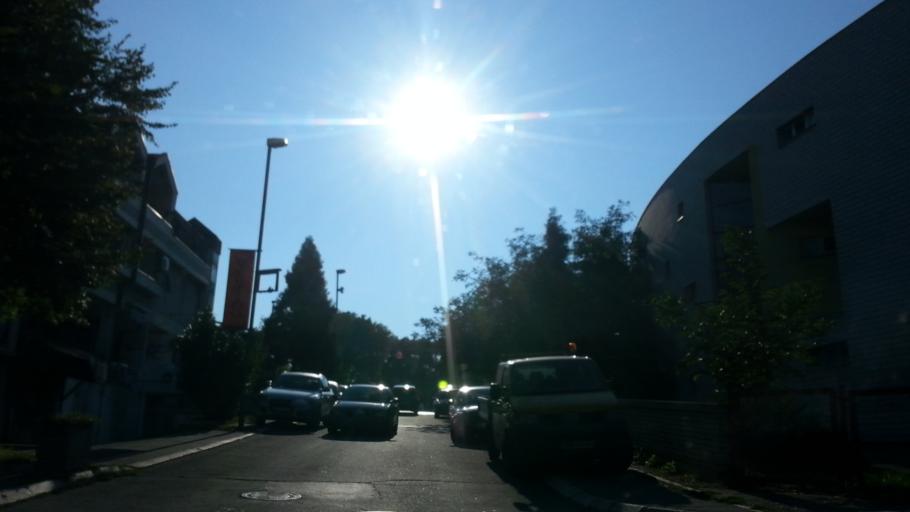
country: RS
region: Central Serbia
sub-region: Belgrade
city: Cukarica
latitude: 44.7660
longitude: 20.4187
